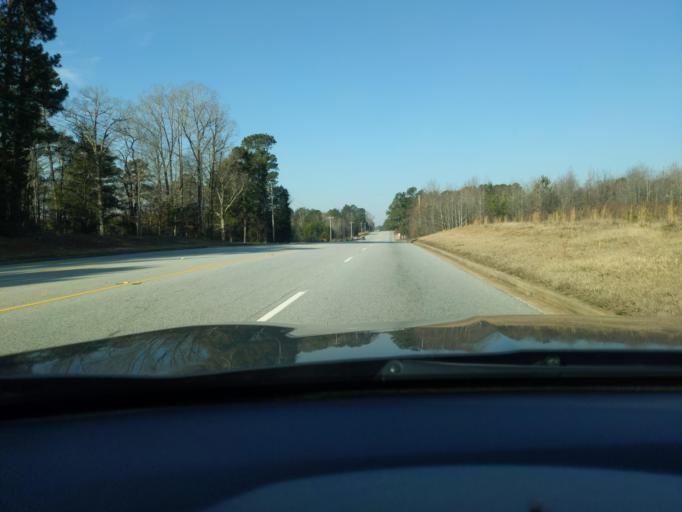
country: US
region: South Carolina
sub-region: Abbeville County
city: Abbeville
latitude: 34.1855
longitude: -82.3369
